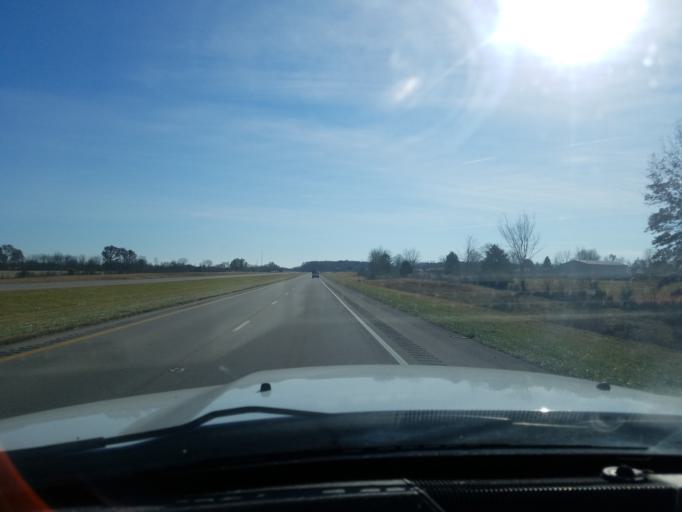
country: US
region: Ohio
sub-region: Adams County
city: Winchester
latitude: 38.9789
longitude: -83.7477
